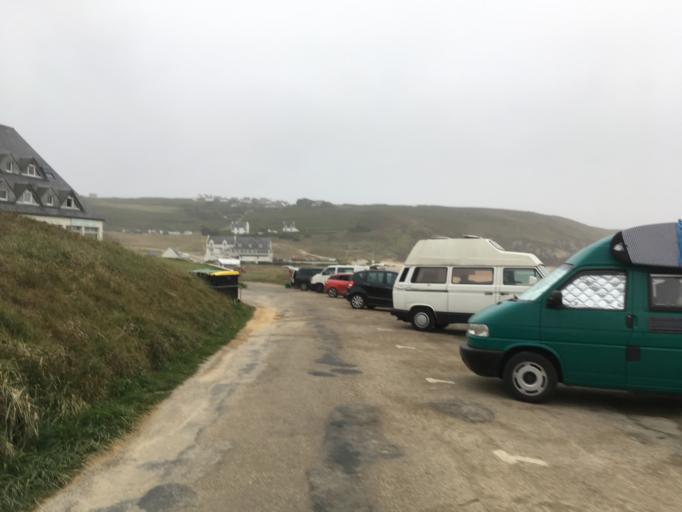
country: FR
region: Brittany
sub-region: Departement du Finistere
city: Plogoff
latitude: 48.0487
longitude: -4.7050
